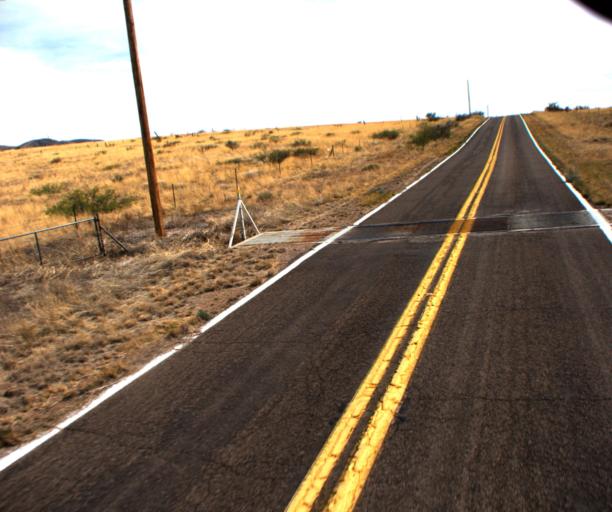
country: US
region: Arizona
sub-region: Cochise County
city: Willcox
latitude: 31.9572
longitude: -109.4772
